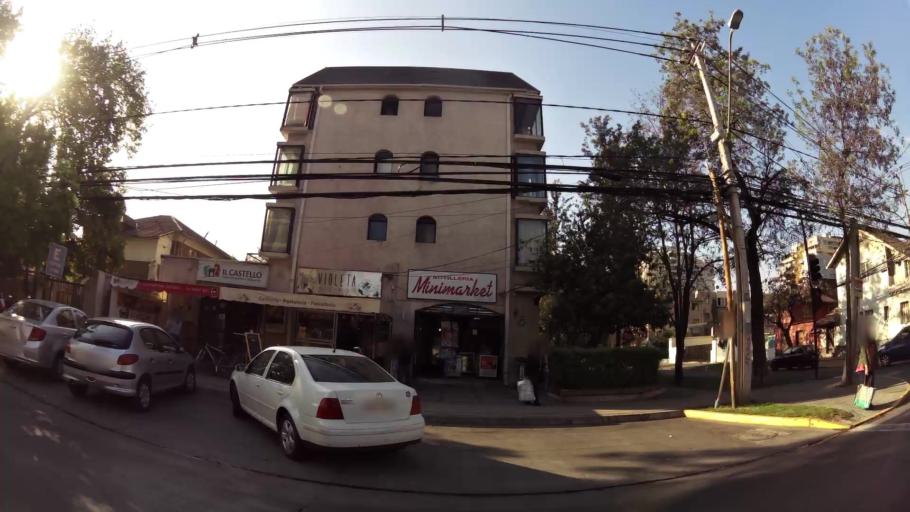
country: CL
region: Santiago Metropolitan
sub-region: Provincia de Santiago
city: Villa Presidente Frei, Nunoa, Santiago, Chile
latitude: -33.4483
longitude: -70.6026
